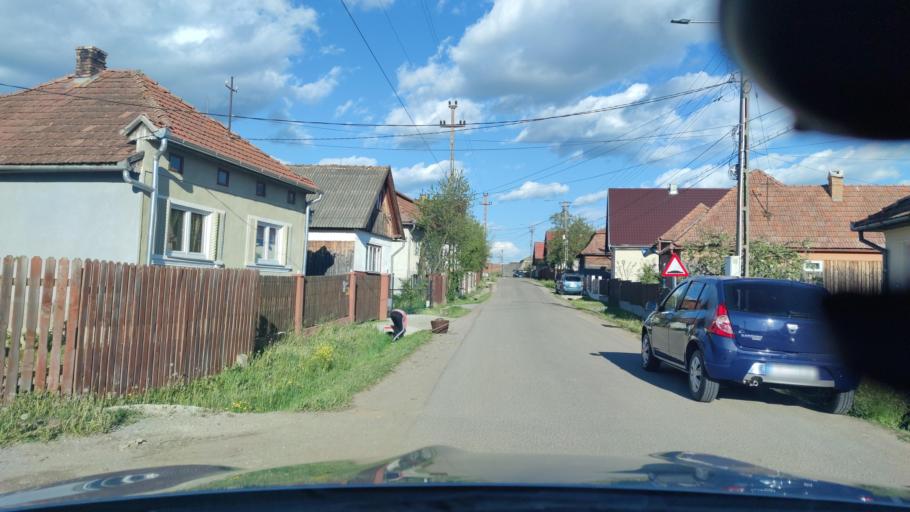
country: RO
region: Harghita
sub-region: Comuna Remetea
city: Remetea
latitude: 46.7994
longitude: 25.4294
